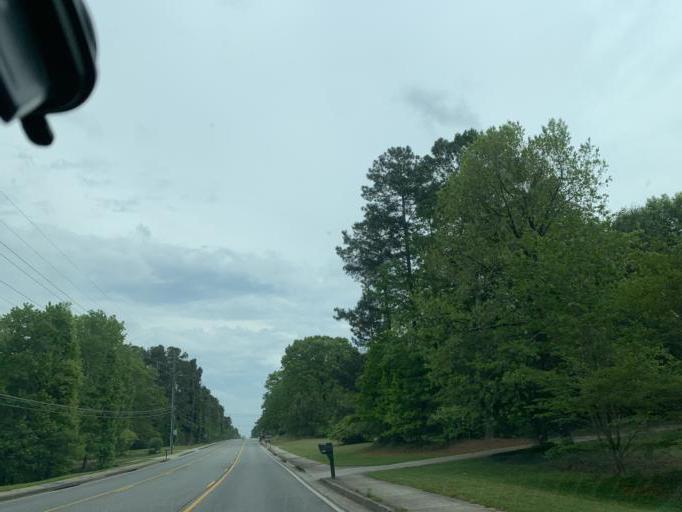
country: US
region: Georgia
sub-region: Forsyth County
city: Cumming
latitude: 34.1977
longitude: -84.1243
